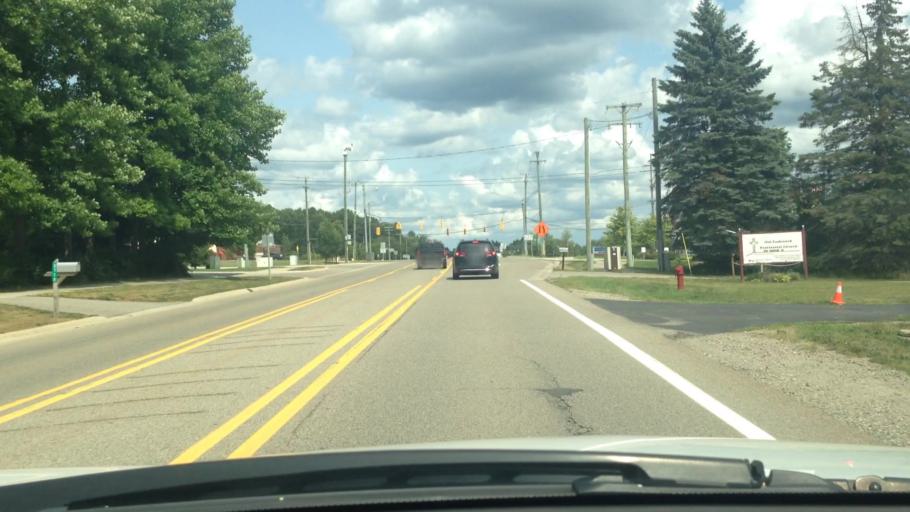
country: US
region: Michigan
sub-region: Oakland County
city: Clarkston
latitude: 42.7517
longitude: -83.3825
